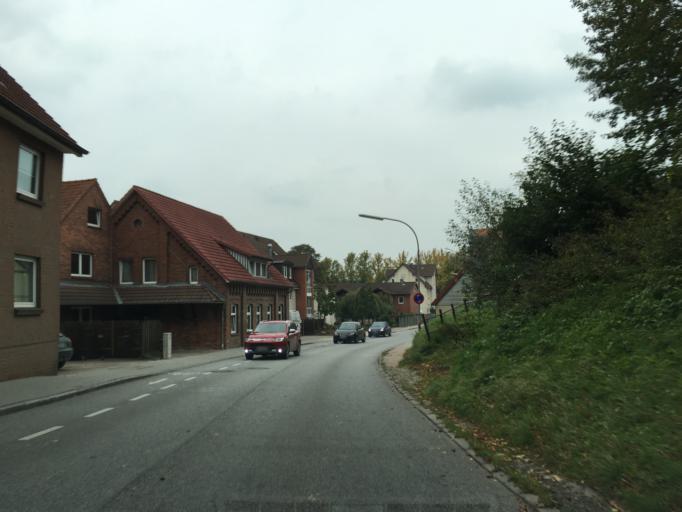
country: DE
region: Schleswig-Holstein
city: Ratzeburg
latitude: 53.6958
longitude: 10.7832
